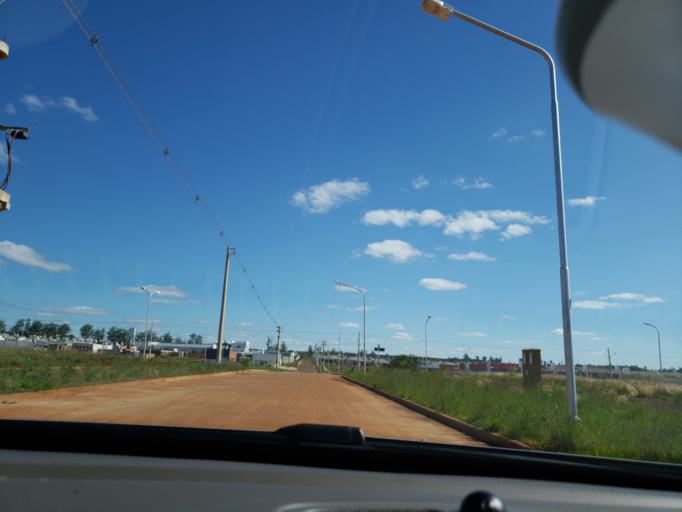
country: AR
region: Misiones
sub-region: Departamento de Capital
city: Posadas
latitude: -27.4068
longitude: -55.9839
